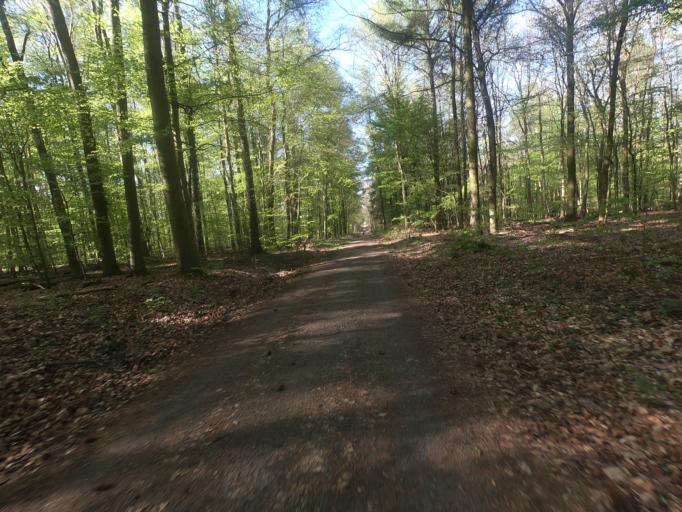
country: DE
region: Hesse
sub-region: Regierungsbezirk Darmstadt
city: Messel
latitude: 49.9327
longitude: 8.7267
